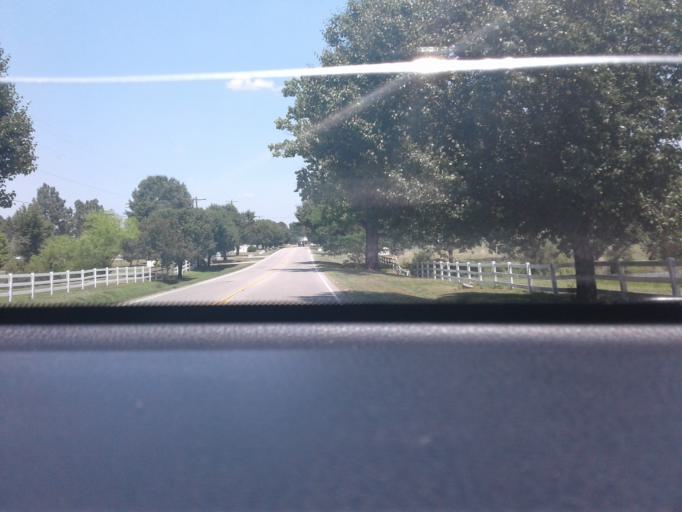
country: US
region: North Carolina
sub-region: Harnett County
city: Dunn
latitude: 35.3386
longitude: -78.5872
